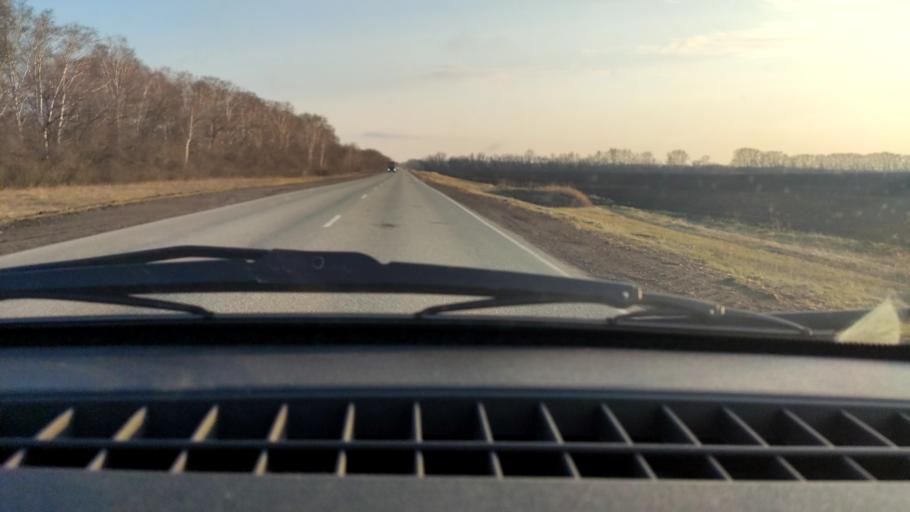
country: RU
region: Bashkortostan
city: Chishmy
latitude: 54.4684
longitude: 55.2606
